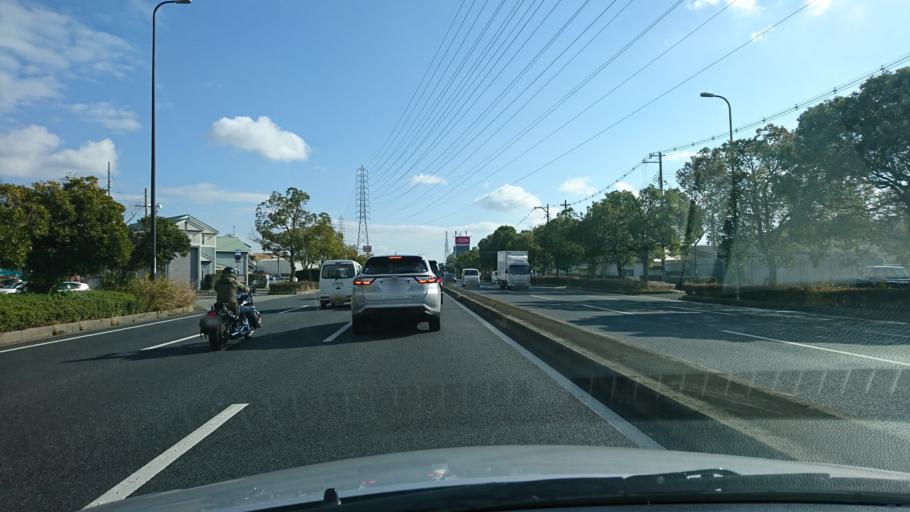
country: JP
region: Hyogo
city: Kakogawacho-honmachi
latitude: 34.7724
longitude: 134.7993
